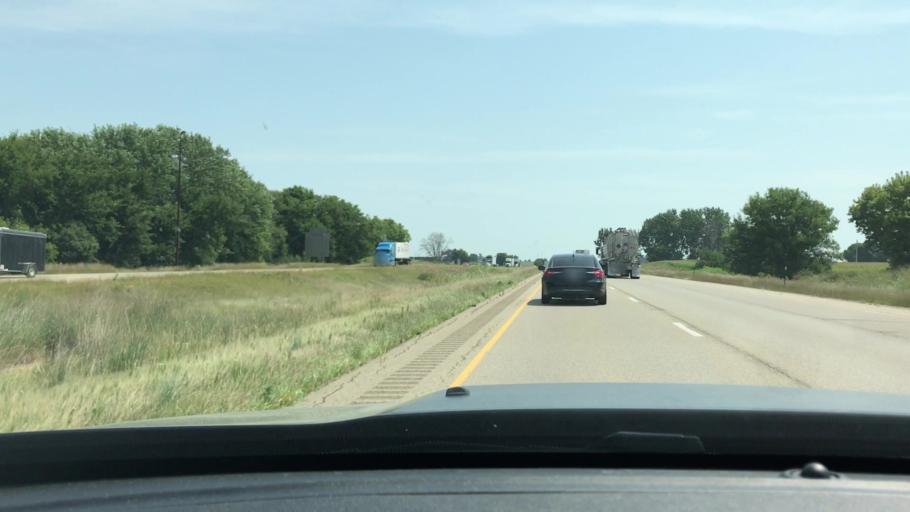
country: US
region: Illinois
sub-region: Bureau County
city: Princeton
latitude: 41.4005
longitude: -89.4641
